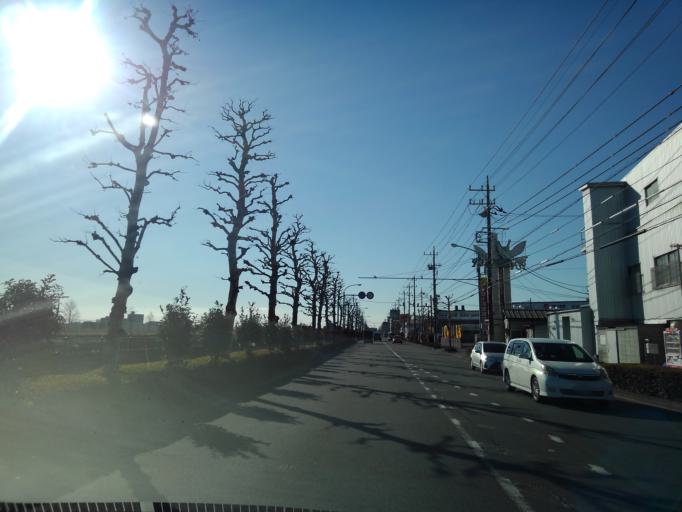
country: JP
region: Tokyo
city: Fussa
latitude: 35.7407
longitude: 139.3829
